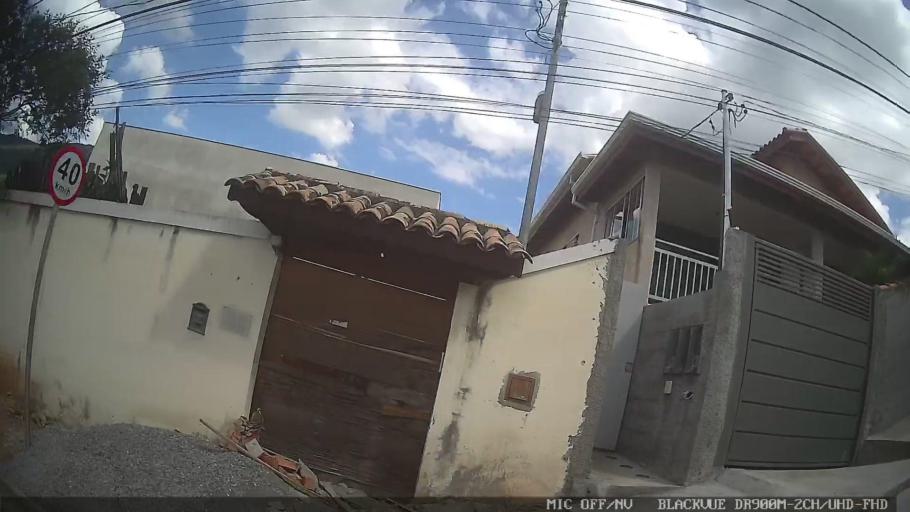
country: BR
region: Minas Gerais
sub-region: Extrema
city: Extrema
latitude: -22.8584
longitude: -46.3169
